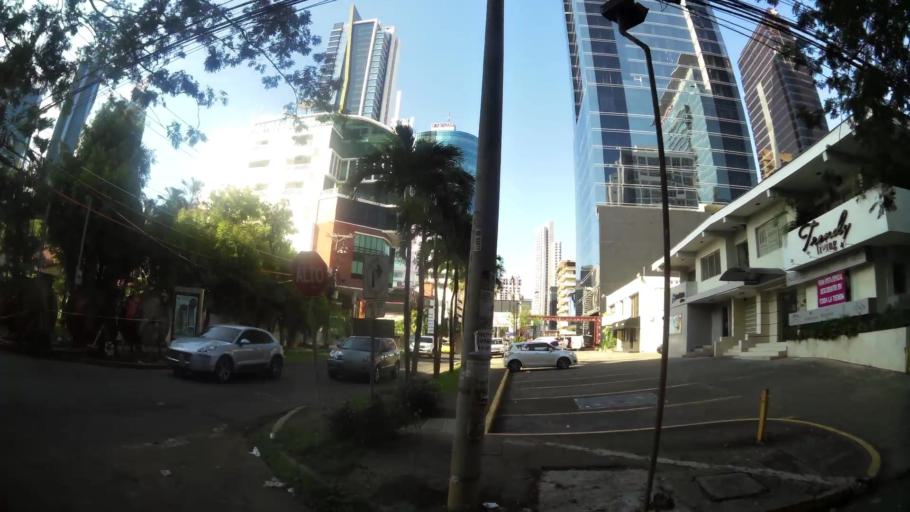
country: PA
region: Panama
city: Panama
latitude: 8.9865
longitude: -79.5203
